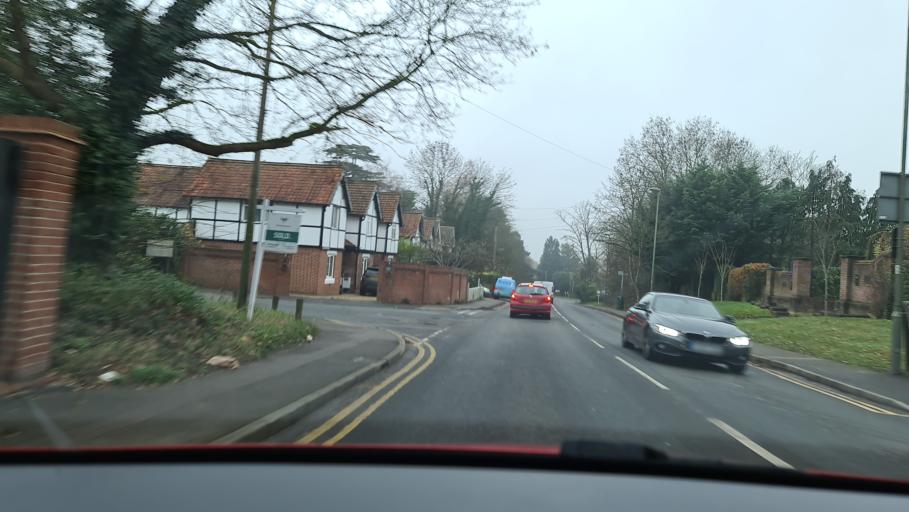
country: GB
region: England
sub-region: Surrey
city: Leatherhead
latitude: 51.3283
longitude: -0.3545
